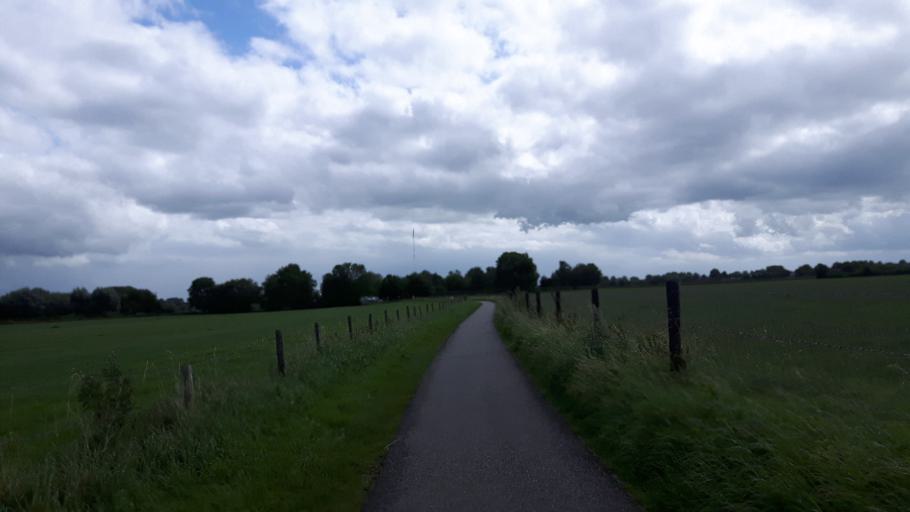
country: NL
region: Utrecht
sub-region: Gemeente IJsselstein
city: IJsselstein
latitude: 52.0397
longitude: 5.0256
